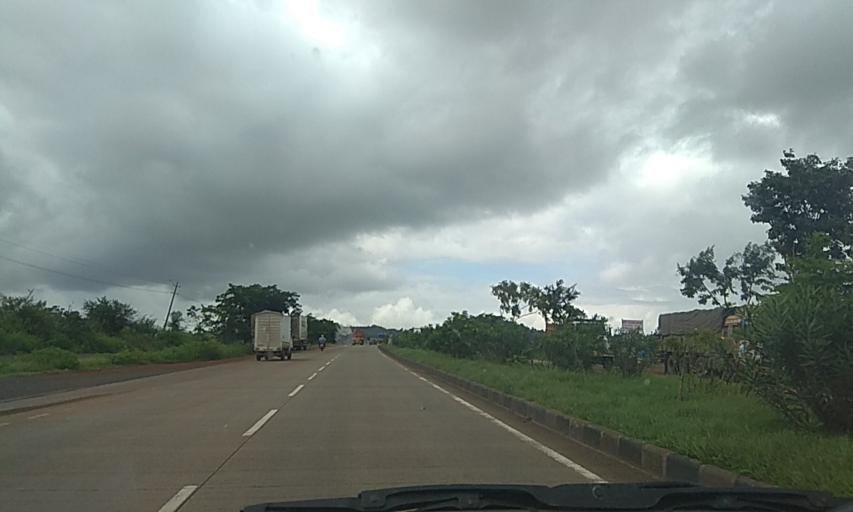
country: IN
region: Karnataka
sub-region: Belgaum
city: Sankeshwar
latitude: 16.2584
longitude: 74.4682
